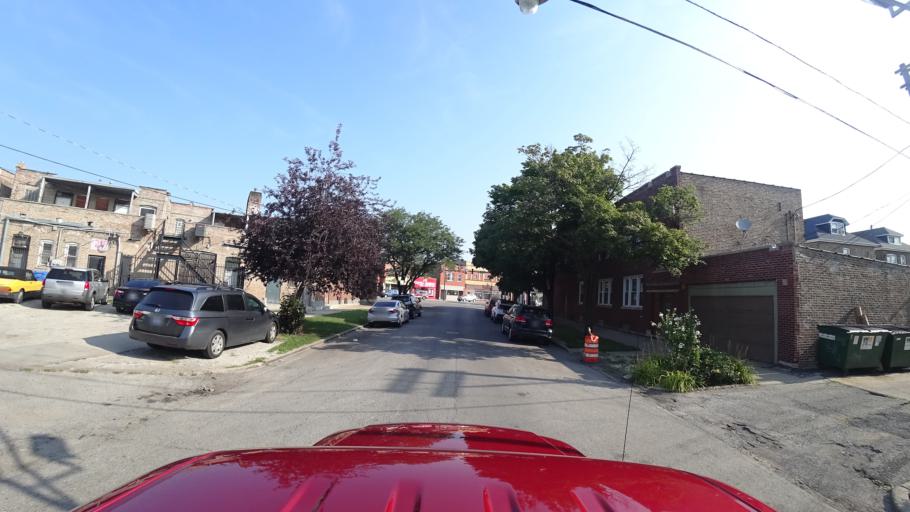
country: US
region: Illinois
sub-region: Cook County
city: Cicero
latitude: 41.8149
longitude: -87.7018
